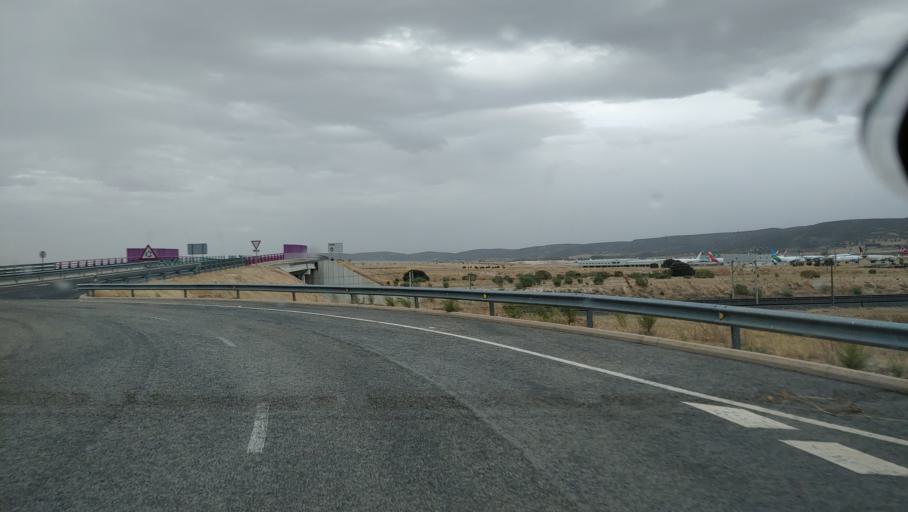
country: ES
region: Castille-La Mancha
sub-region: Provincia de Ciudad Real
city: Canada de Calatrava
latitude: 38.8732
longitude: -3.9929
